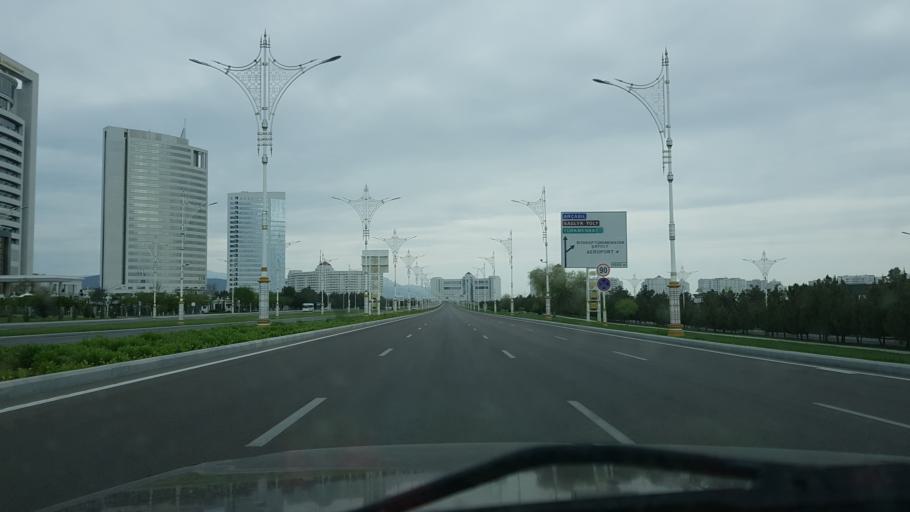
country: TM
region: Ahal
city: Ashgabat
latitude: 37.8893
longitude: 58.3491
